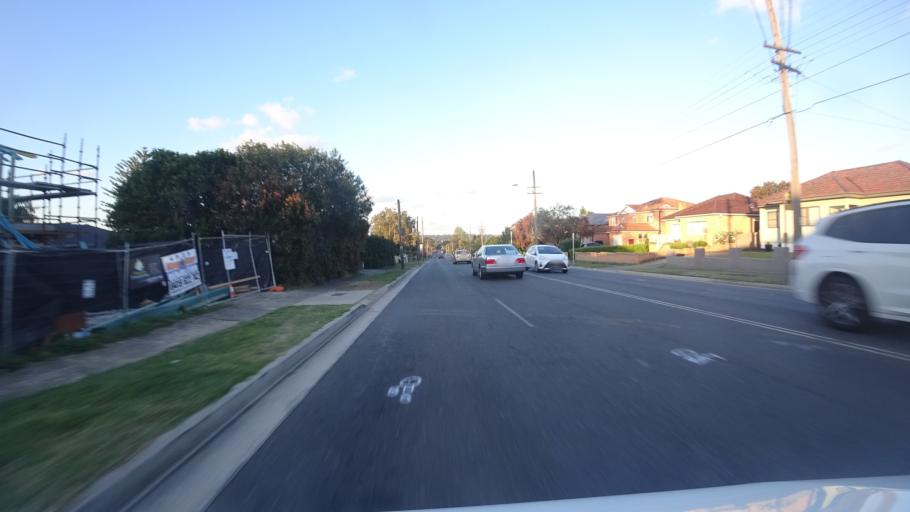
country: AU
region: New South Wales
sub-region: Ryde
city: North Ryde
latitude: -33.7956
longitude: 151.1256
